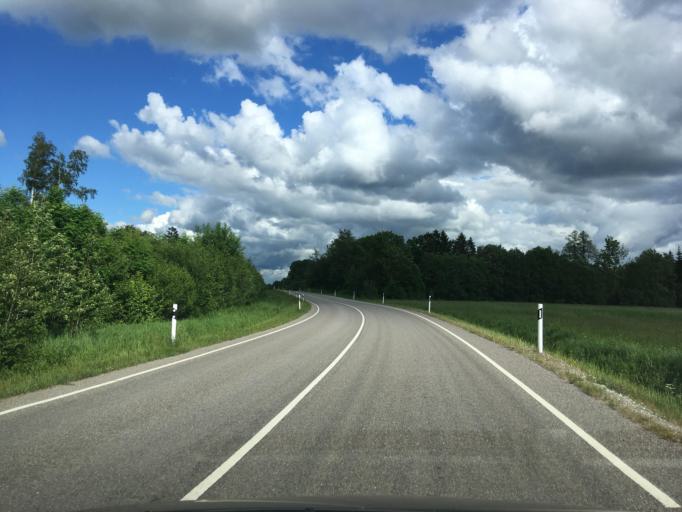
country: EE
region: Paernumaa
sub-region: Tootsi vald
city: Tootsi
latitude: 58.6555
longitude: 24.6932
